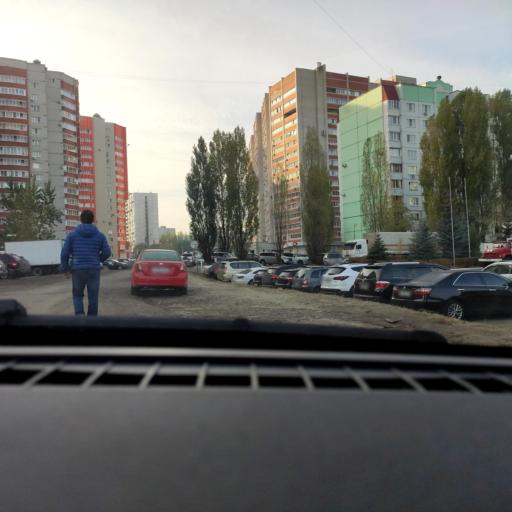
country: RU
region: Voronezj
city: Podgornoye
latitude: 51.7142
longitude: 39.1536
